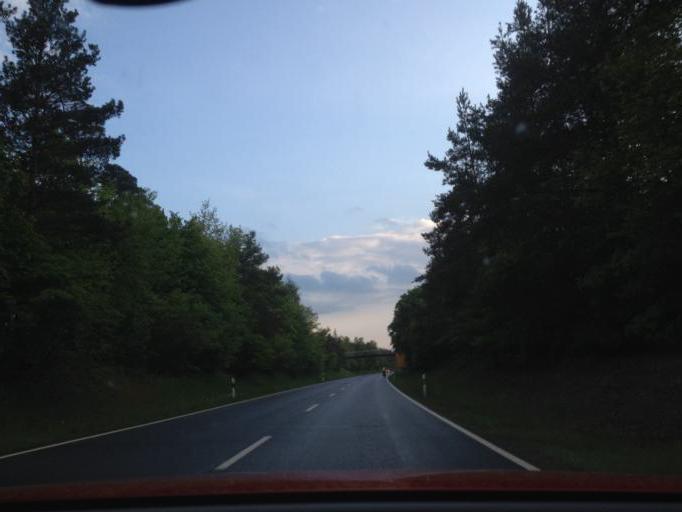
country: DE
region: Bavaria
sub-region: Upper Palatinate
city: Etzenricht
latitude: 49.6193
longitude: 12.0902
